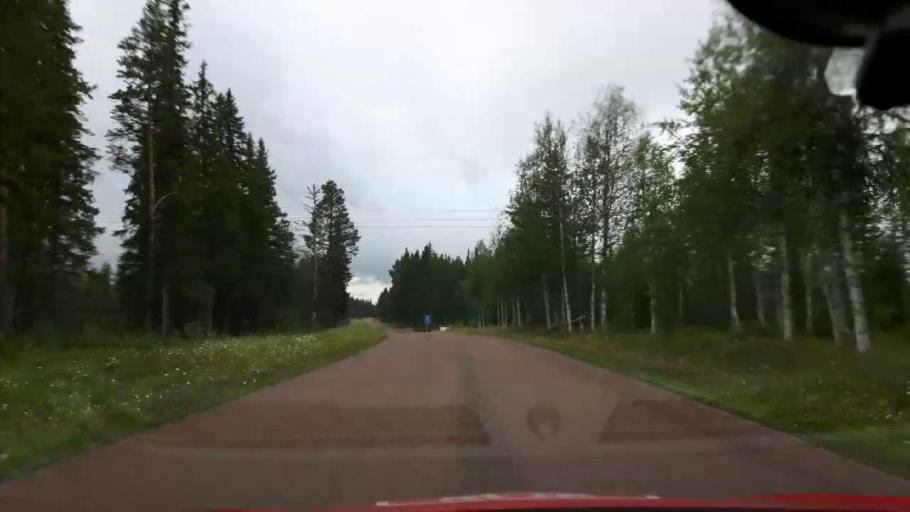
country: SE
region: Jaemtland
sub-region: Krokoms Kommun
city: Valla
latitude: 63.3600
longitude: 13.7319
